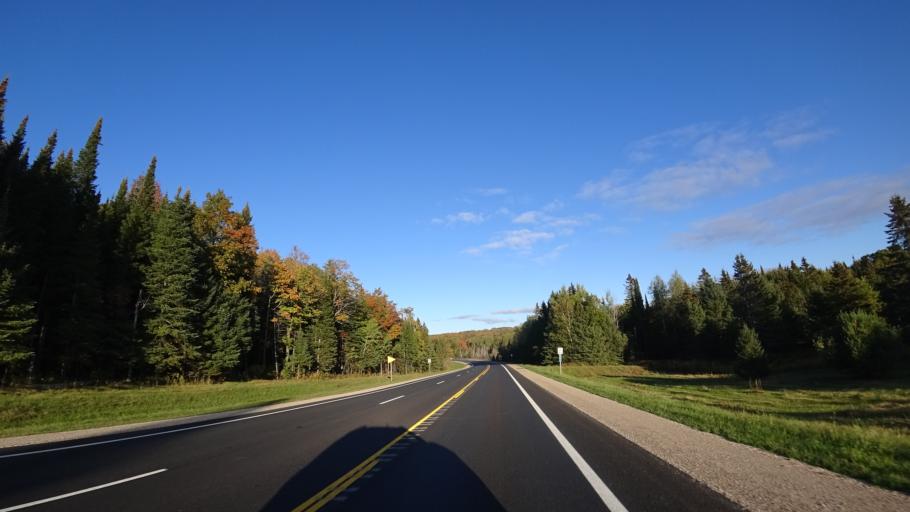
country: US
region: Michigan
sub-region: Luce County
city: Newberry
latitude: 46.3358
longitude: -85.7572
